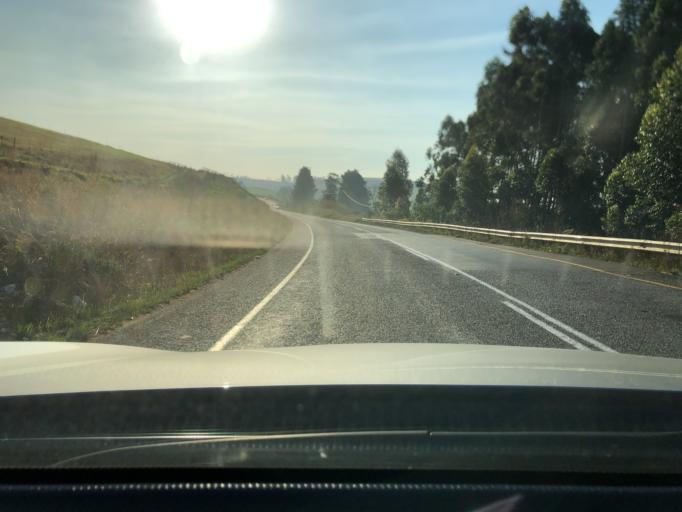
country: ZA
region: KwaZulu-Natal
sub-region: Sisonke District Municipality
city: Ixopo
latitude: -30.2502
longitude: 30.1871
